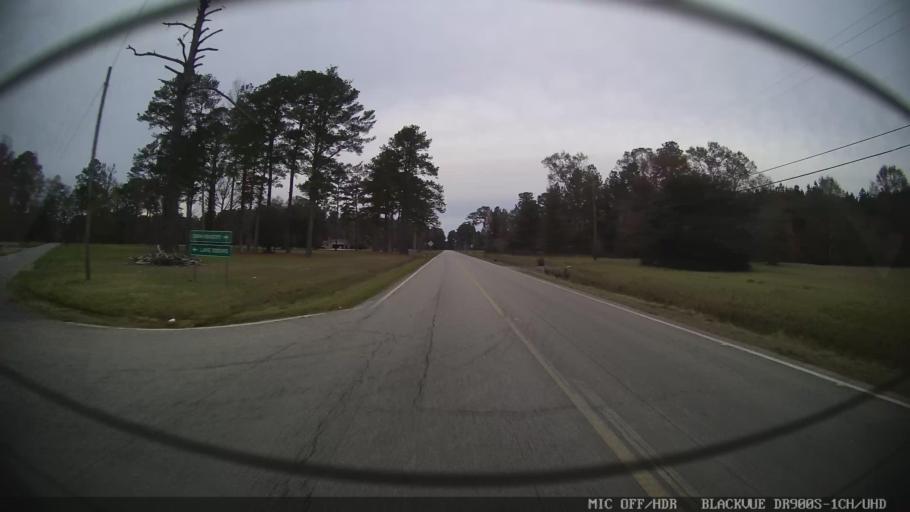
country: US
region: Mississippi
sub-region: Clarke County
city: Stonewall
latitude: 32.0431
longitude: -88.8894
